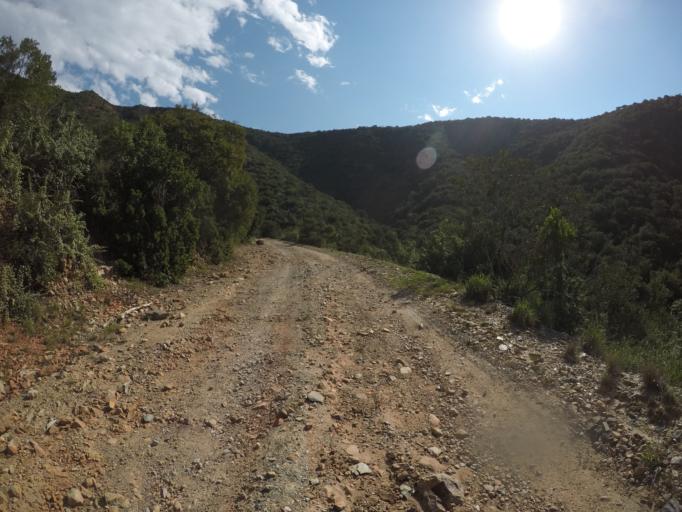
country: ZA
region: Eastern Cape
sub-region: Cacadu District Municipality
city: Kareedouw
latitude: -33.6518
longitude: 24.3477
